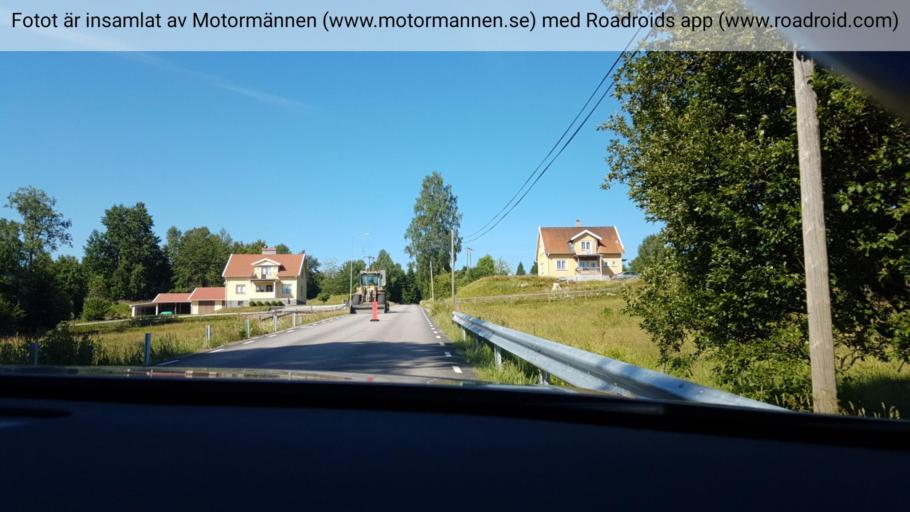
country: SE
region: Vaestra Goetaland
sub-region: Ulricehamns Kommun
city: Ulricehamn
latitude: 57.8598
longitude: 13.4196
